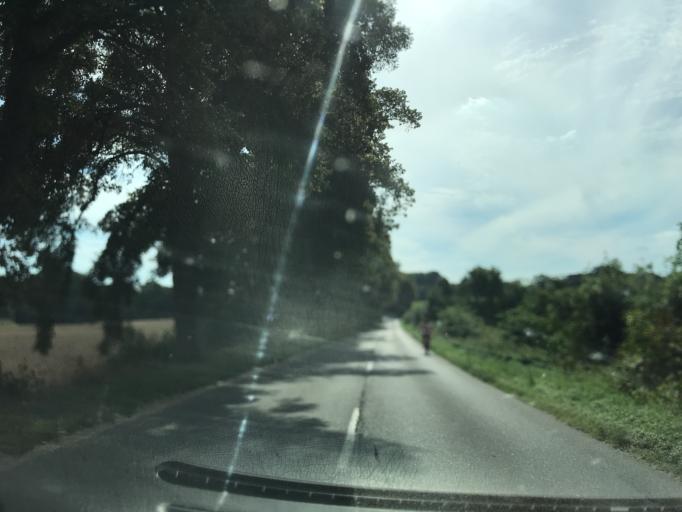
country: PL
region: Pomeranian Voivodeship
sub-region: Powiat pucki
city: Krokowa
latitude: 54.7718
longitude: 18.1626
